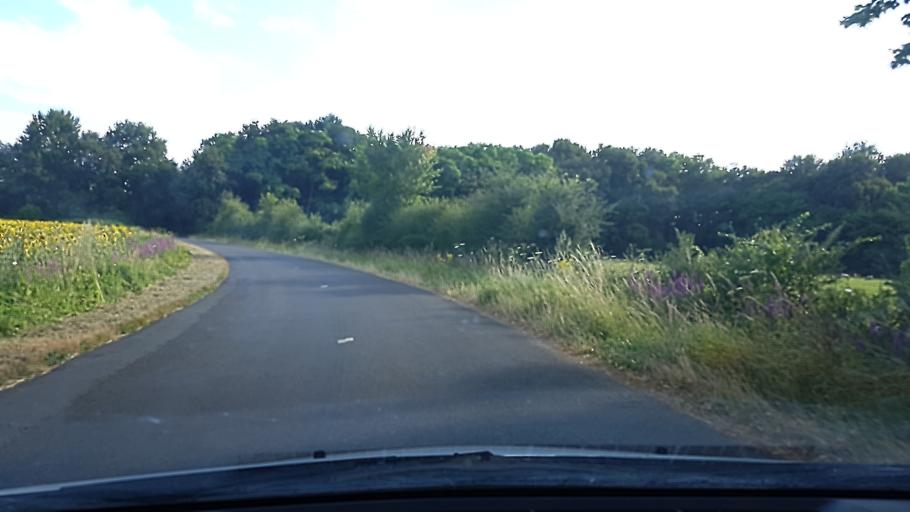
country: FR
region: Pays de la Loire
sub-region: Departement de Maine-et-Loire
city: Jarze
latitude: 47.5179
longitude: -0.2154
